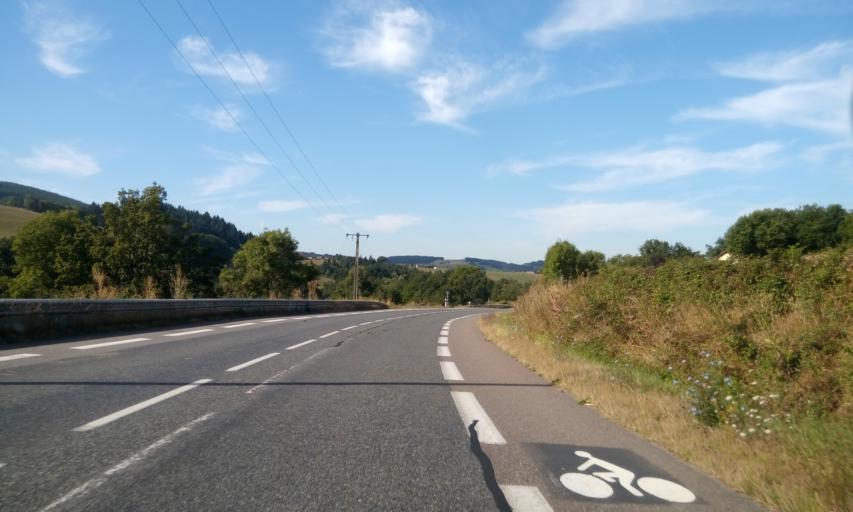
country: FR
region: Rhone-Alpes
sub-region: Departement du Rhone
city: Amplepuis
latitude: 45.9747
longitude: 4.3621
